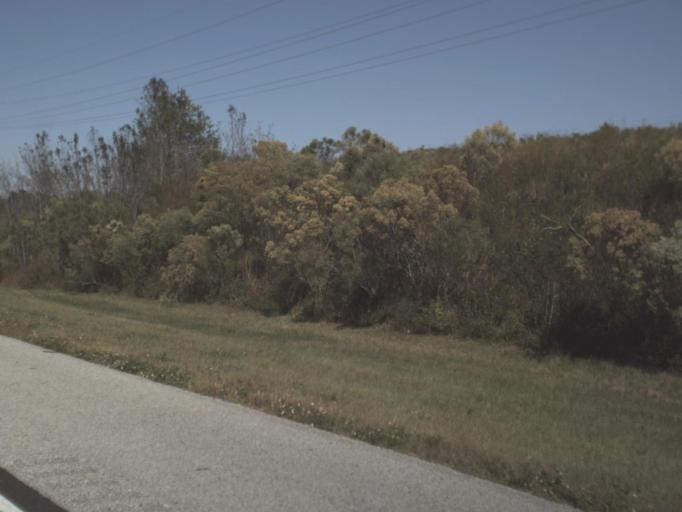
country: US
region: Florida
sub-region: Lake County
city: Hawthorne
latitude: 28.7644
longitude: -81.9481
